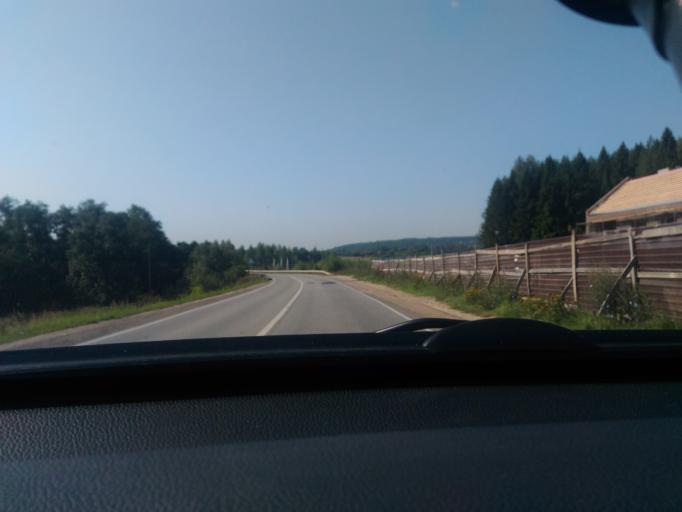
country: RU
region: Moskovskaya
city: Podosinki
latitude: 56.2139
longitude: 37.5438
